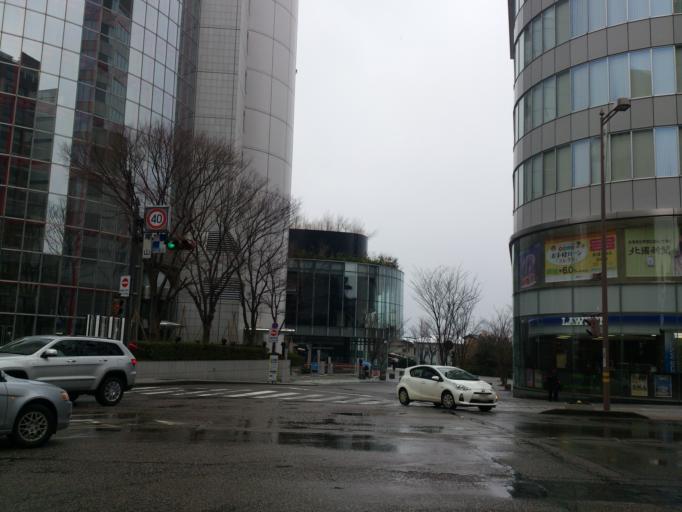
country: JP
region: Ishikawa
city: Kanazawa-shi
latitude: 36.5652
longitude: 136.6537
